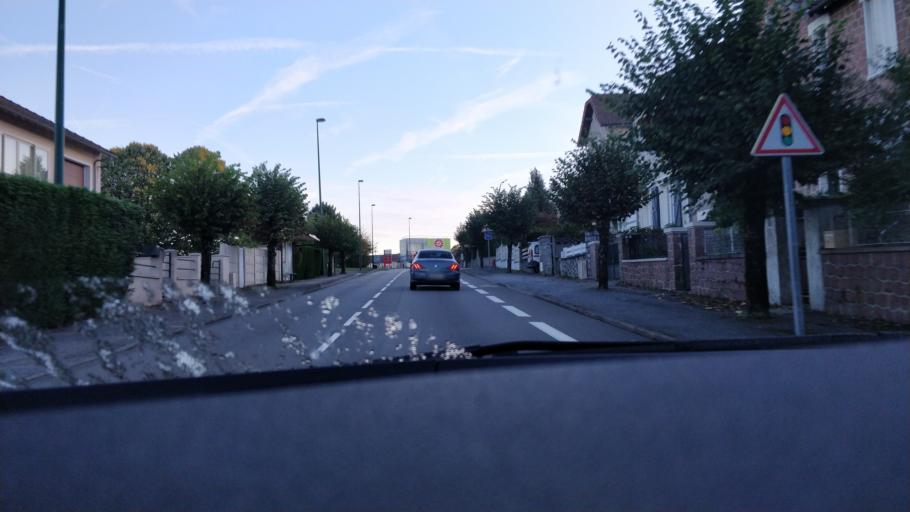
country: FR
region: Limousin
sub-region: Departement de la Haute-Vienne
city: Limoges
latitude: 45.8262
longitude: 1.2911
